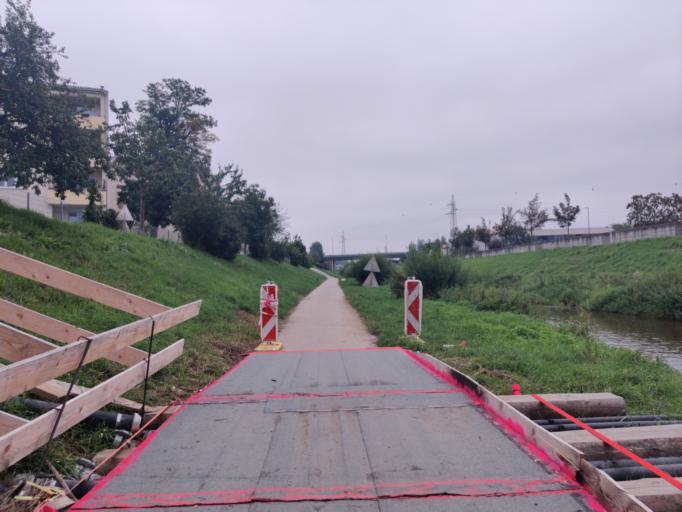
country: AT
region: Lower Austria
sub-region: Krems an der Donau Stadt
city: Krems an der Donau
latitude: 48.4108
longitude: 15.6214
